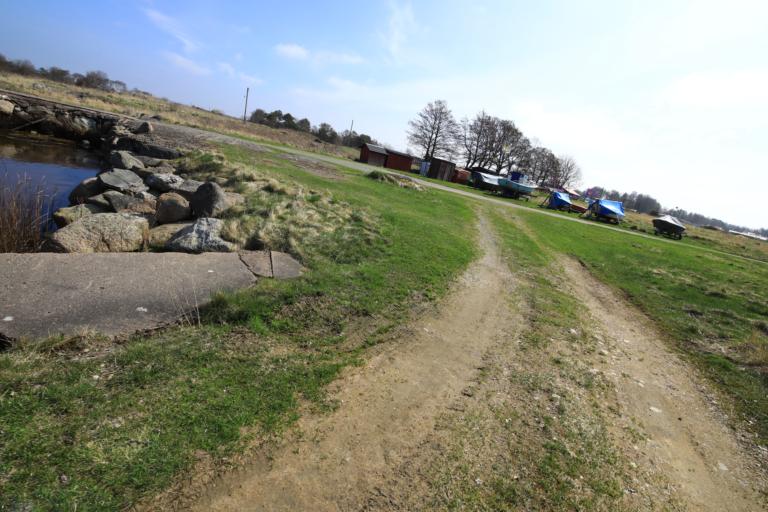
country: SE
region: Halland
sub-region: Kungsbacka Kommun
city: Frillesas
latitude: 57.2806
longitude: 12.1385
